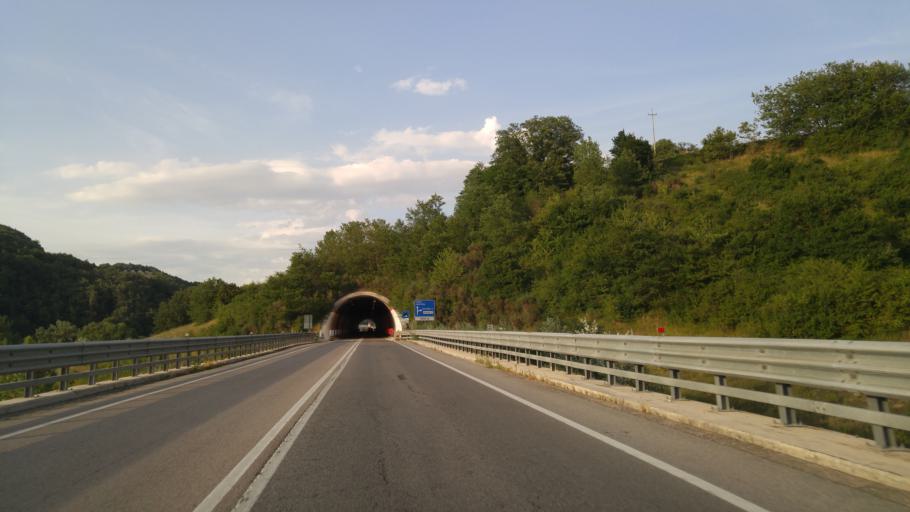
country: IT
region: Umbria
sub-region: Provincia di Perugia
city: Nocera Umbra
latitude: 43.0956
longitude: 12.7688
